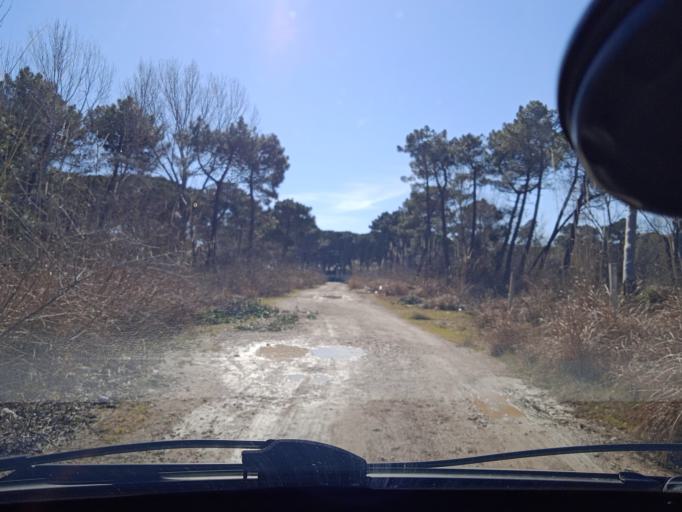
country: AL
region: Shkoder
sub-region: Rrethi i Shkodres
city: Velipoje
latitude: 41.8651
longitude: 19.4189
